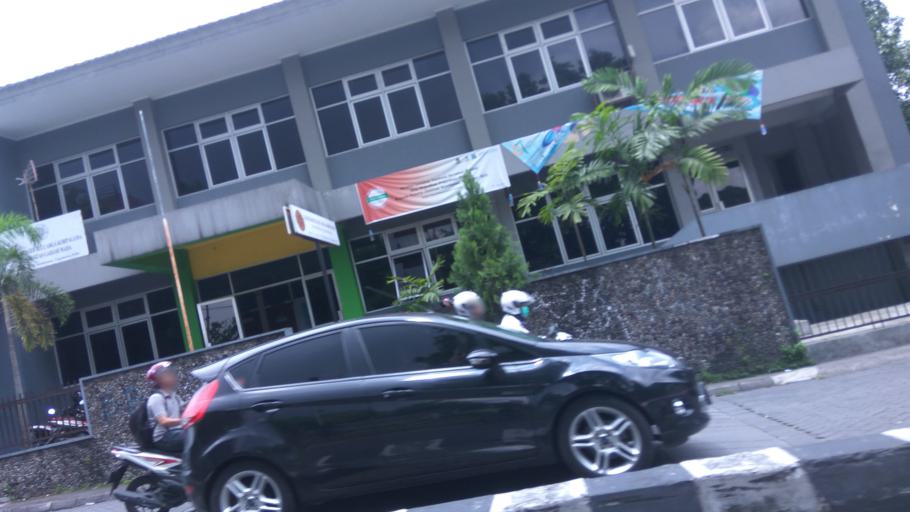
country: ID
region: Daerah Istimewa Yogyakarta
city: Yogyakarta
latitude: -7.7670
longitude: 110.3824
